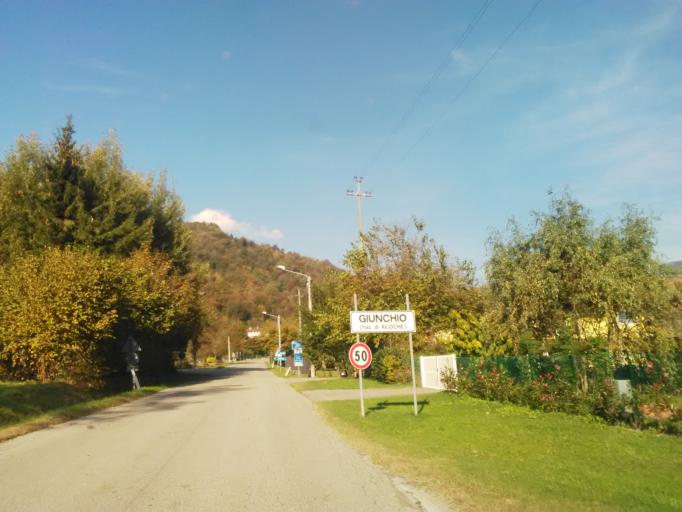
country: IT
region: Piedmont
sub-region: Provincia di Vercelli
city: Guardabosone
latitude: 45.7002
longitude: 8.2377
